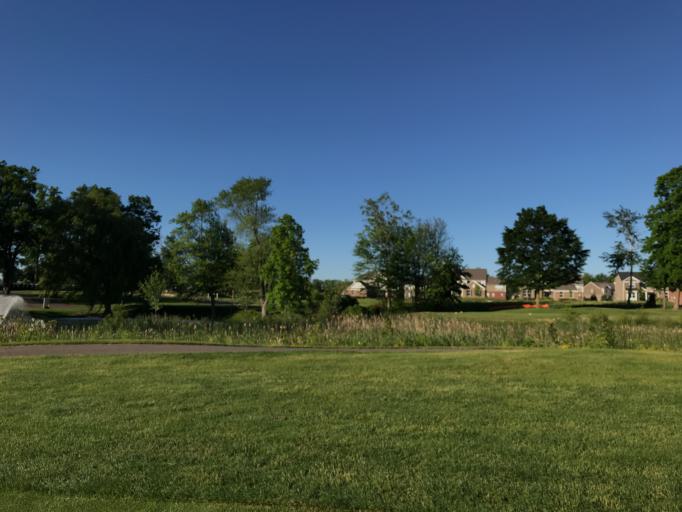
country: US
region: Michigan
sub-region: Oakland County
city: South Lyon
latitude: 42.4539
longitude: -83.5783
